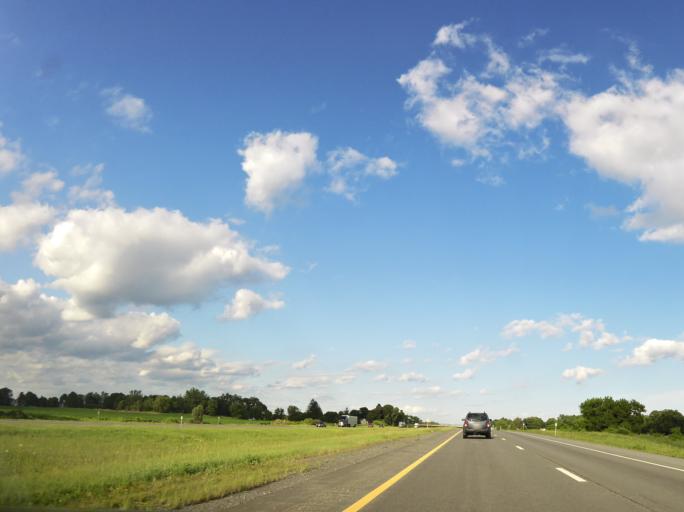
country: US
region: New York
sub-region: Genesee County
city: Batavia
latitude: 43.0173
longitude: -78.2265
